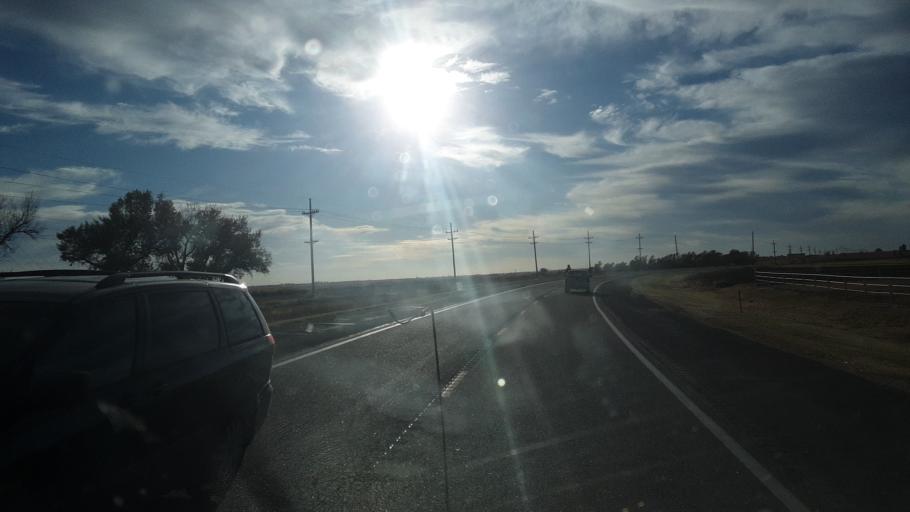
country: US
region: Kansas
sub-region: Kearny County
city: Lakin
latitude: 37.9745
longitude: -101.1493
